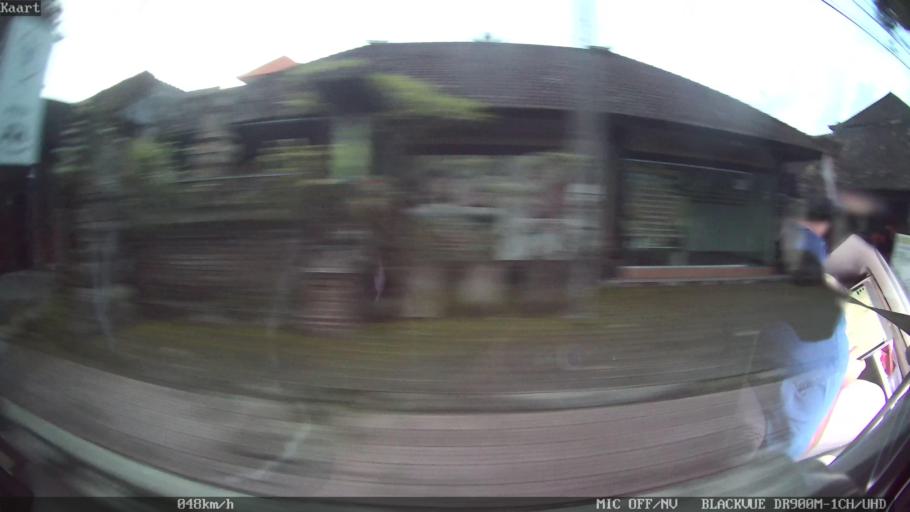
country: ID
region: Bali
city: Pegongan
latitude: -8.4871
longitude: 115.2463
